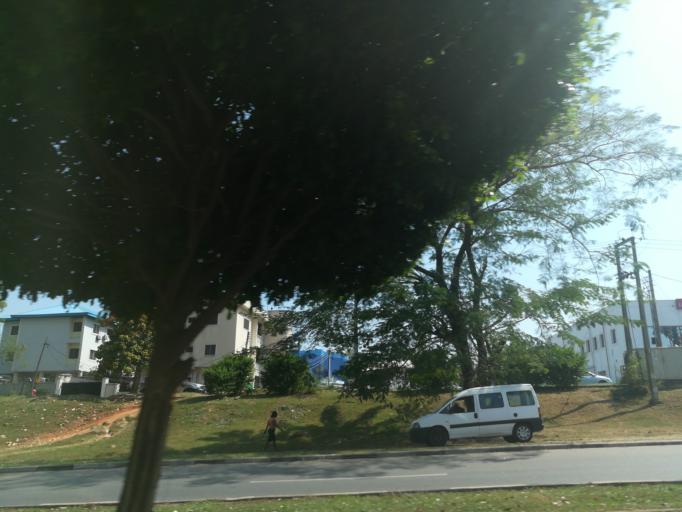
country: NG
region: Abuja Federal Capital Territory
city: Abuja
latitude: 9.0574
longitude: 7.4592
